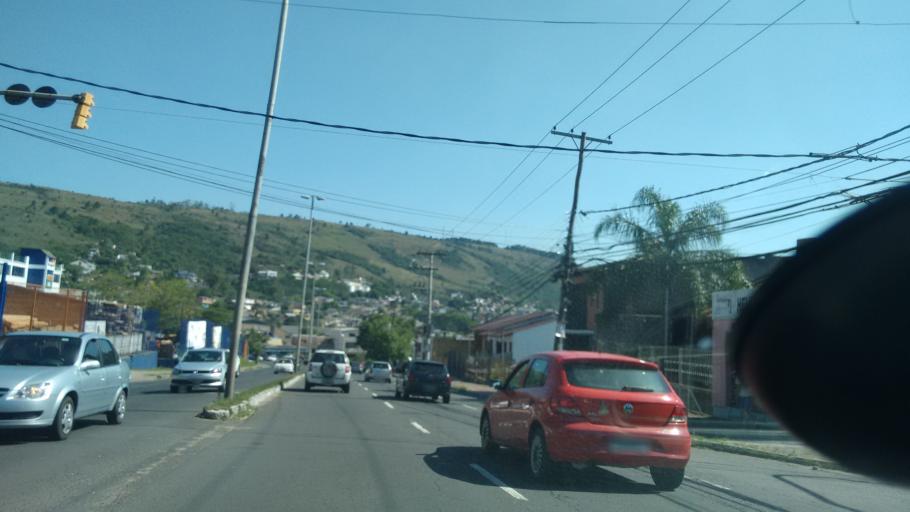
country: BR
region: Rio Grande do Sul
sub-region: Cachoeirinha
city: Cachoeirinha
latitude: -30.0371
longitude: -51.1221
